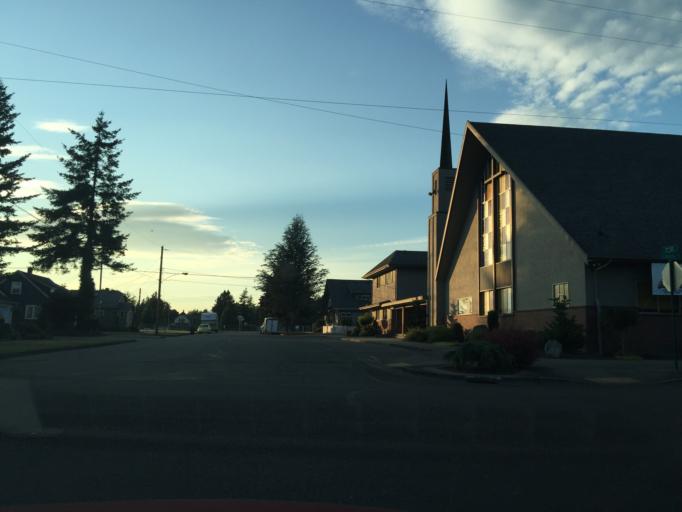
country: US
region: Washington
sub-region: Whatcom County
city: Lynden
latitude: 48.9439
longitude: -122.4568
